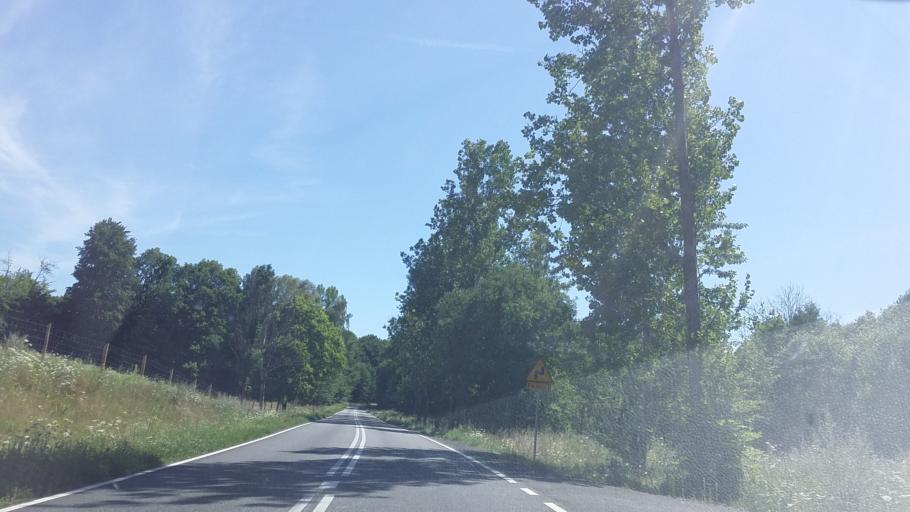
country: PL
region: West Pomeranian Voivodeship
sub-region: Powiat lobeski
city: Wegorzyno
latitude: 53.4911
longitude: 15.5796
